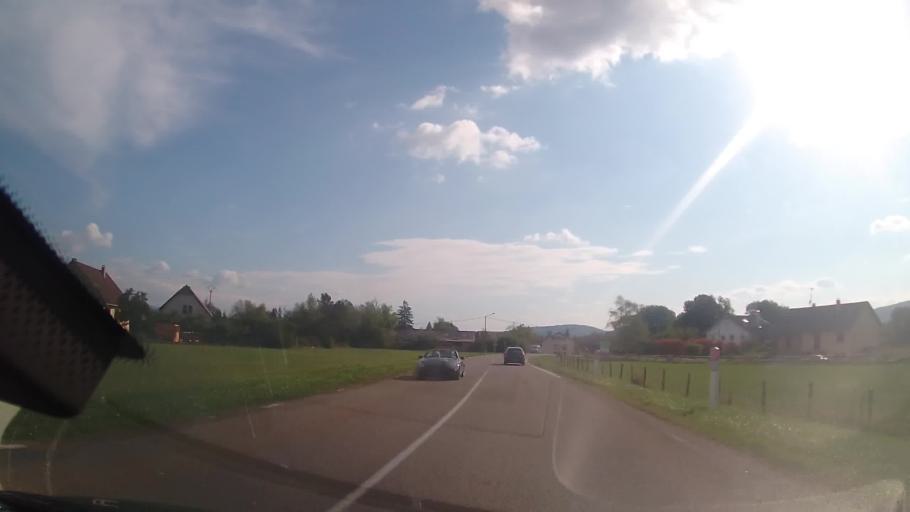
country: FR
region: Franche-Comte
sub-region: Departement du Jura
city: Clairvaux-les-Lacs
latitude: 46.5886
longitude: 5.7071
